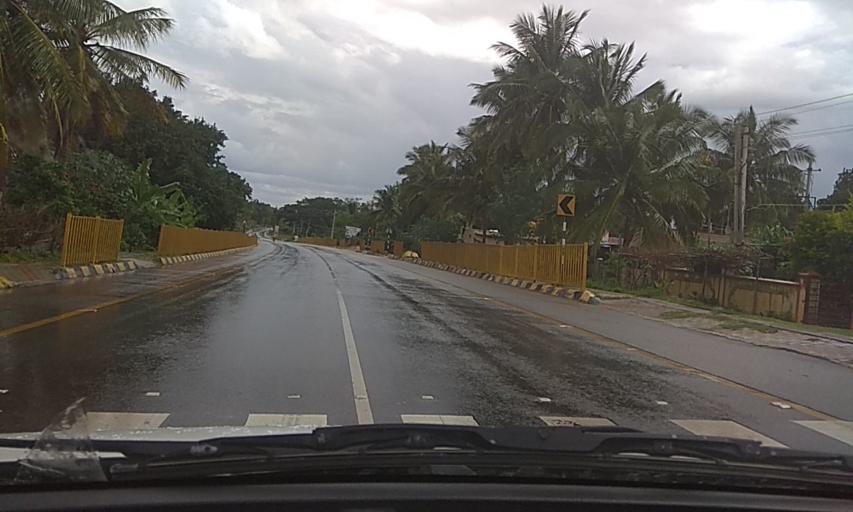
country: IN
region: Karnataka
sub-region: Tumkur
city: Kunigal
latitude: 13.1106
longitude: 77.0260
